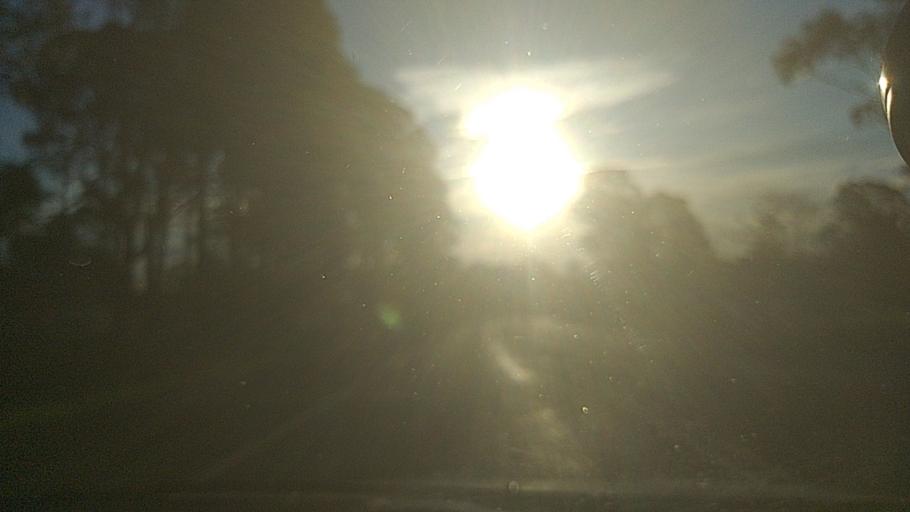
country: AU
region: New South Wales
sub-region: Wollondilly
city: Douglas Park
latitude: -34.2416
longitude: 150.7126
